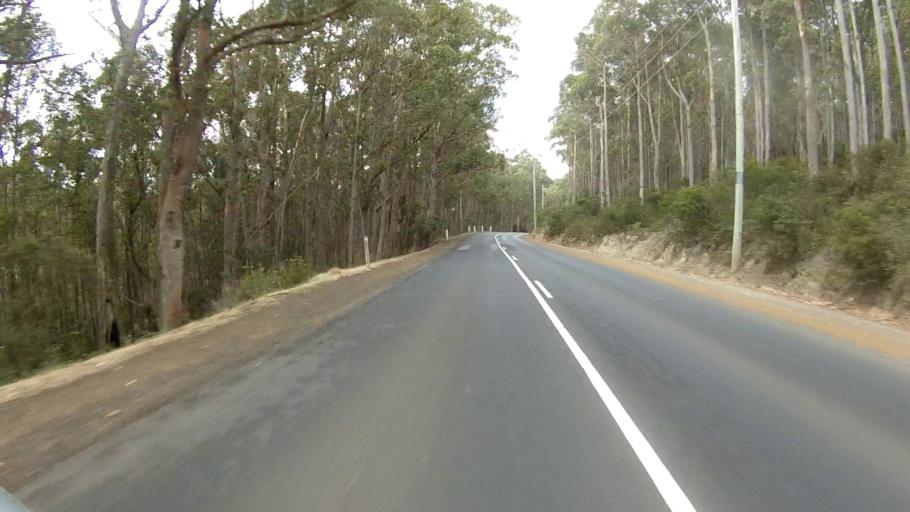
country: AU
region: Tasmania
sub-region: Hobart
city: Dynnyrne
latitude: -42.9099
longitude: 147.2715
